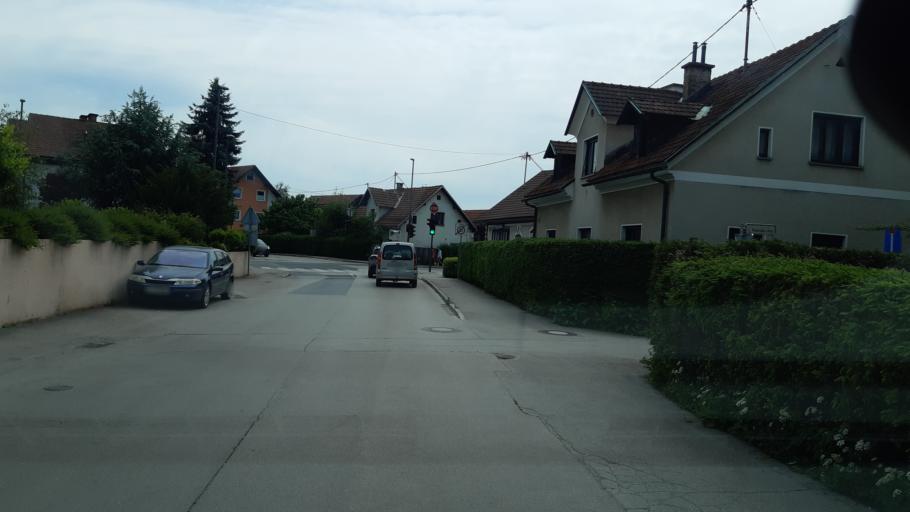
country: SI
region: Ljubljana
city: Ljubljana
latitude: 46.0821
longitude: 14.4718
